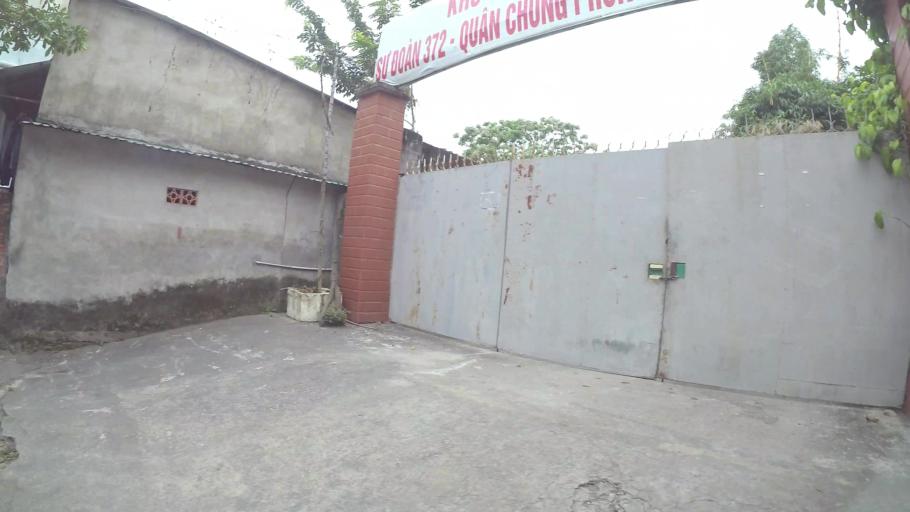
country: VN
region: Da Nang
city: Cam Le
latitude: 16.0446
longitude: 108.2059
